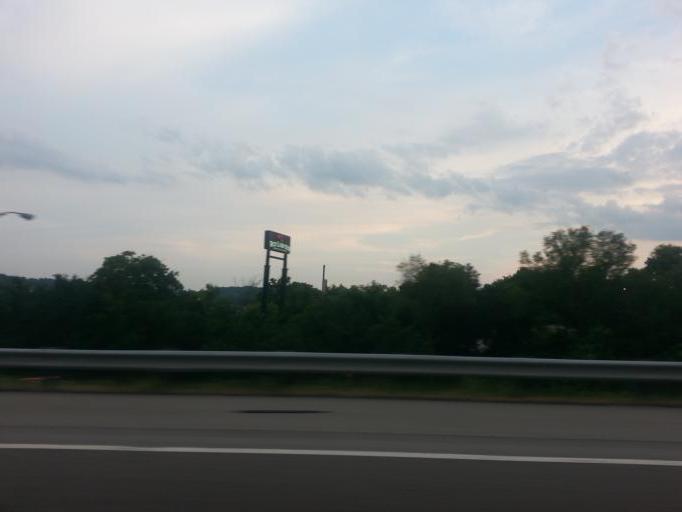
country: US
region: Tennessee
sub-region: Knox County
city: Knoxville
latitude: 36.0117
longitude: -83.9748
